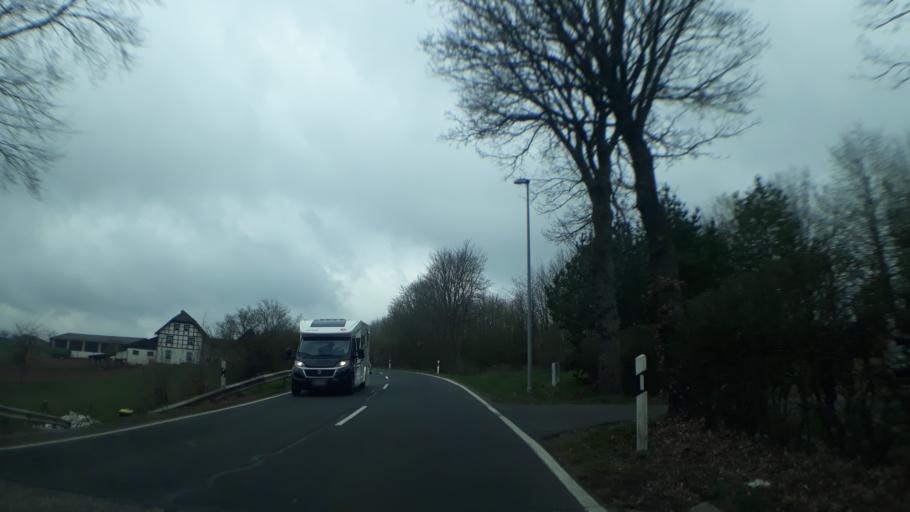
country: DE
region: North Rhine-Westphalia
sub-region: Regierungsbezirk Koln
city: Schleiden
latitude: 50.5527
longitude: 6.4625
